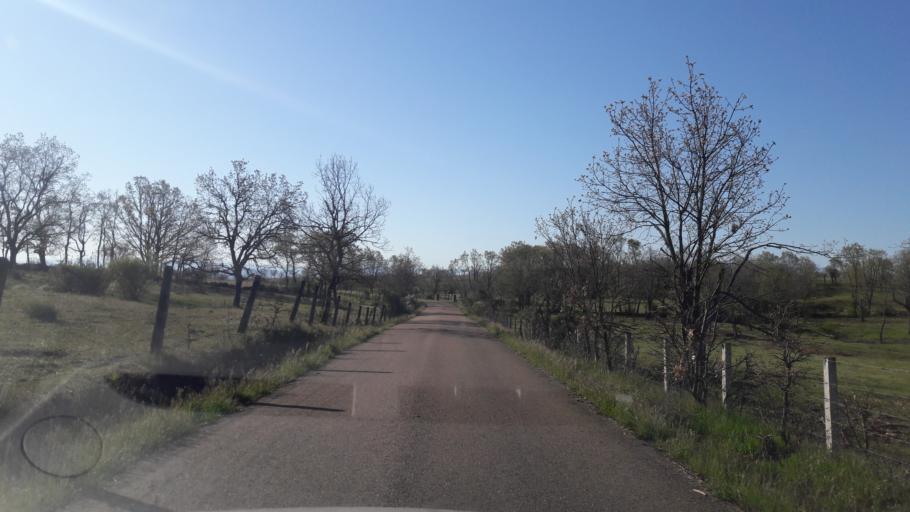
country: ES
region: Castille and Leon
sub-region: Provincia de Salamanca
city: Herguijuela del Campo
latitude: 40.6353
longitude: -5.8900
